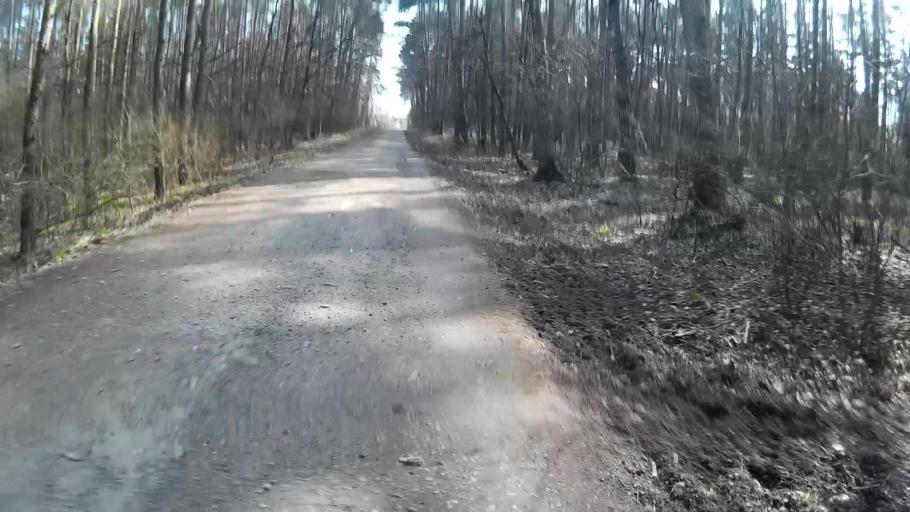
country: CZ
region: South Moravian
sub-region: Mesto Brno
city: Mokra Hora
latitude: 49.2598
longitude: 16.6149
